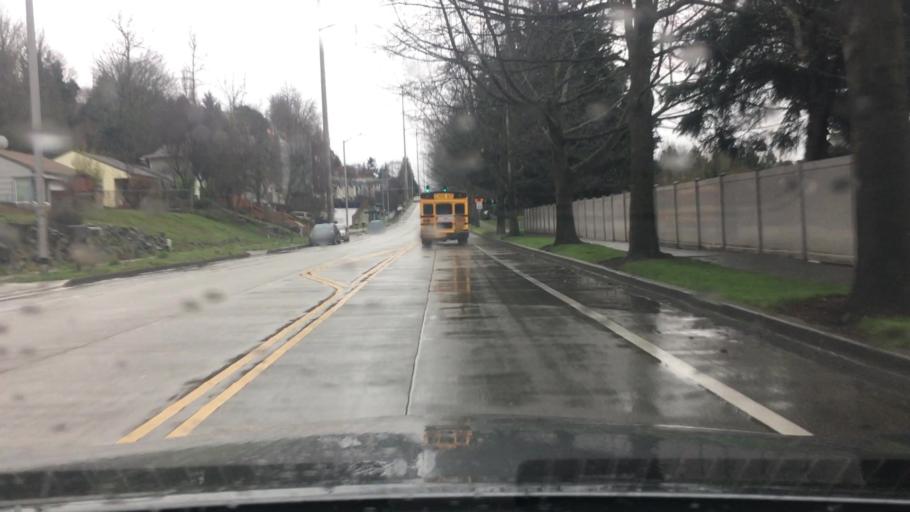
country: US
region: Washington
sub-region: King County
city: White Center
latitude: 47.5334
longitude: -122.3605
